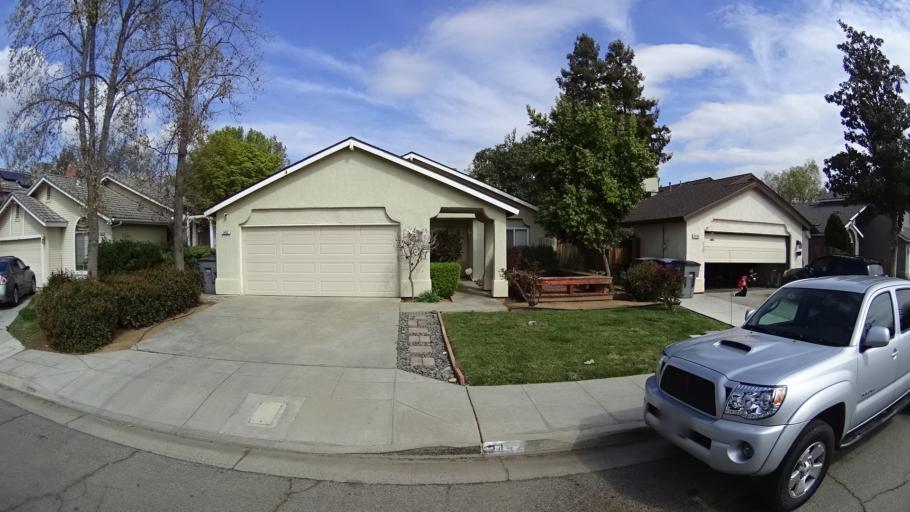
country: US
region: California
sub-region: Fresno County
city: West Park
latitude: 36.8171
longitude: -119.8542
